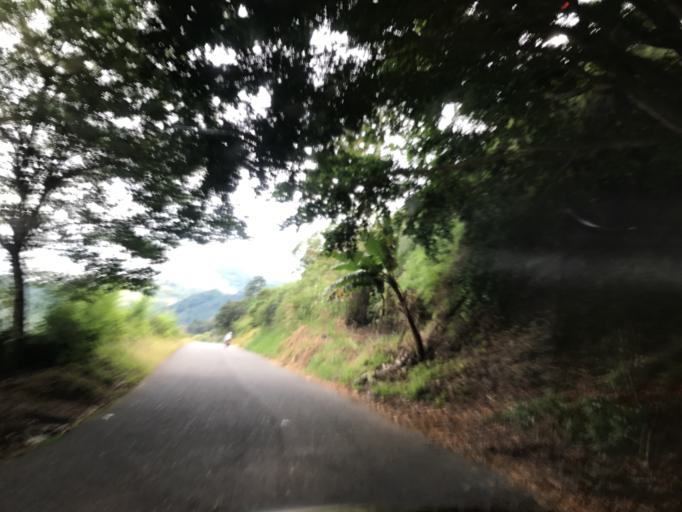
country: CO
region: Quindio
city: Buenavista
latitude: 4.3661
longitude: -75.7488
